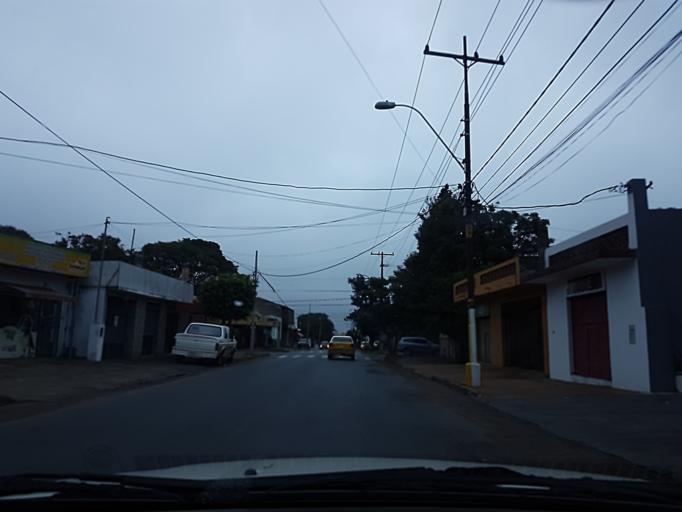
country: PY
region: Central
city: Fernando de la Mora
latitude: -25.2911
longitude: -57.5688
